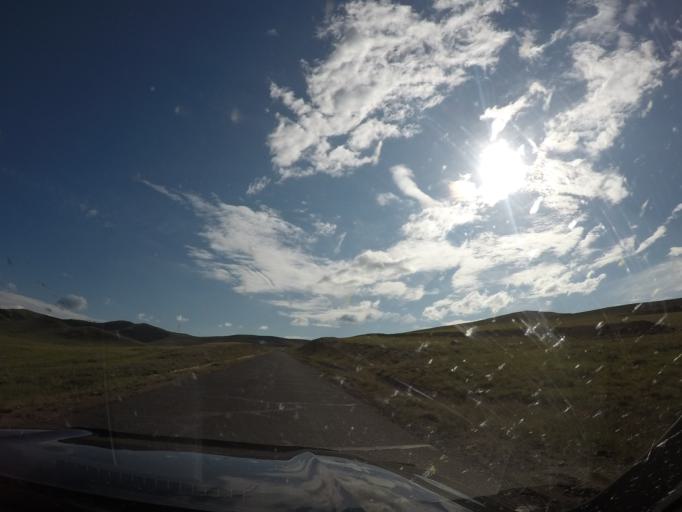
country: MN
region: Hentiy
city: Modot
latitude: 47.8002
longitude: 108.7753
